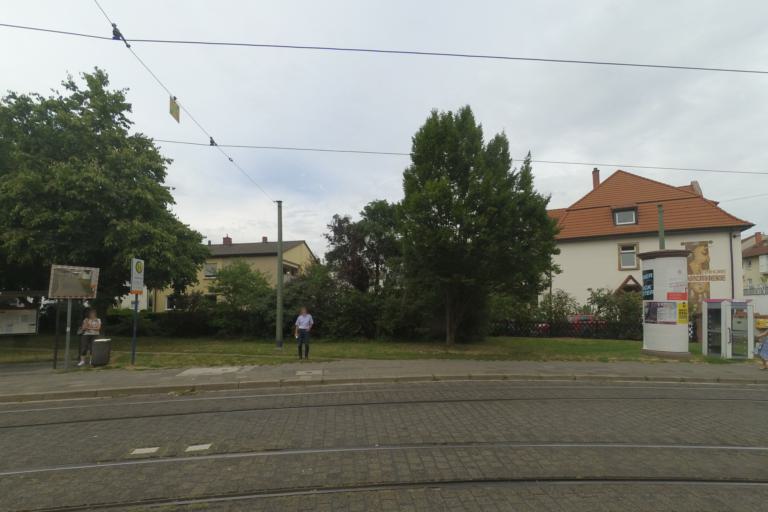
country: DE
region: Rheinland-Pfalz
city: Ludwigshafen am Rhein
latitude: 49.4992
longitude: 8.4163
